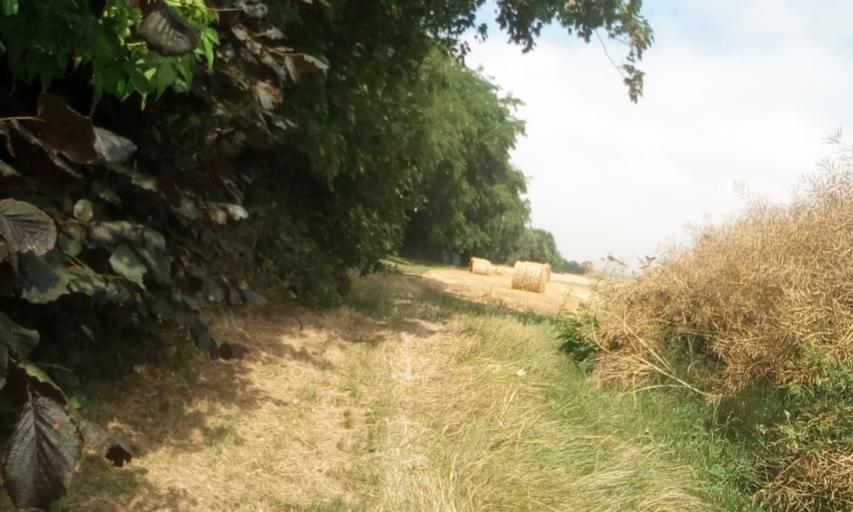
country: FR
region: Lower Normandy
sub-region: Departement du Calvados
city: Douvres-la-Delivrande
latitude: 49.2959
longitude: -0.4103
